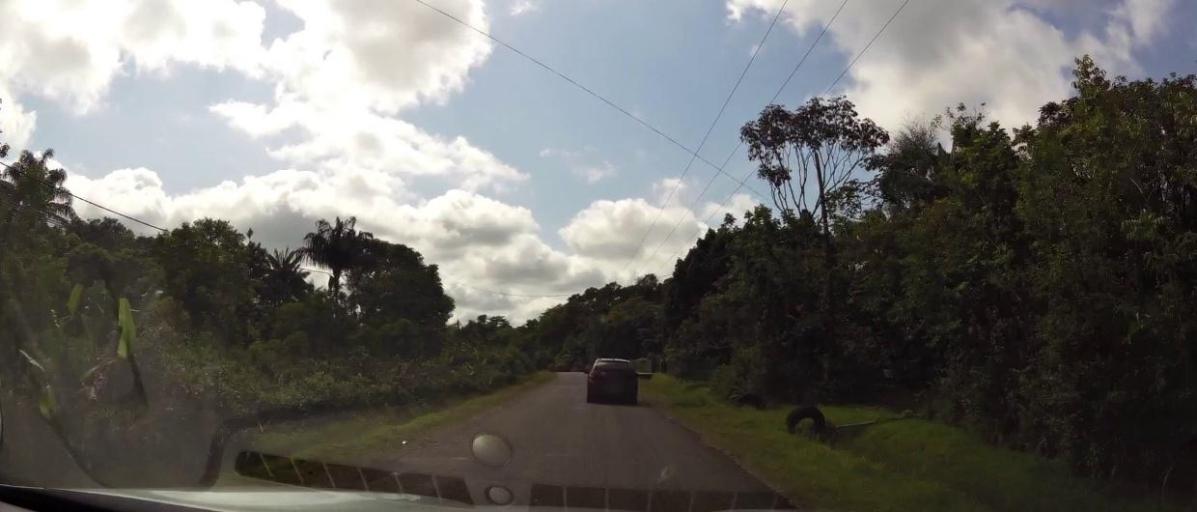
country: GF
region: Guyane
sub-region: Guyane
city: Matoury
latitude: 4.8303
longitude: -52.3127
